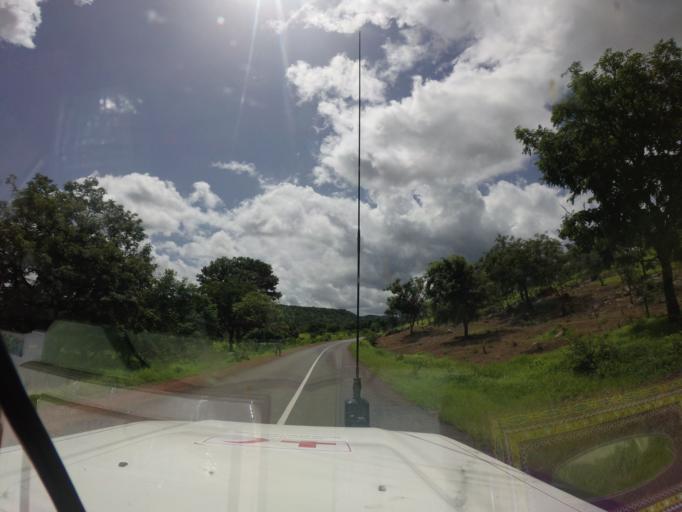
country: SL
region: Northern Province
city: Bindi
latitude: 10.1487
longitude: -11.6706
